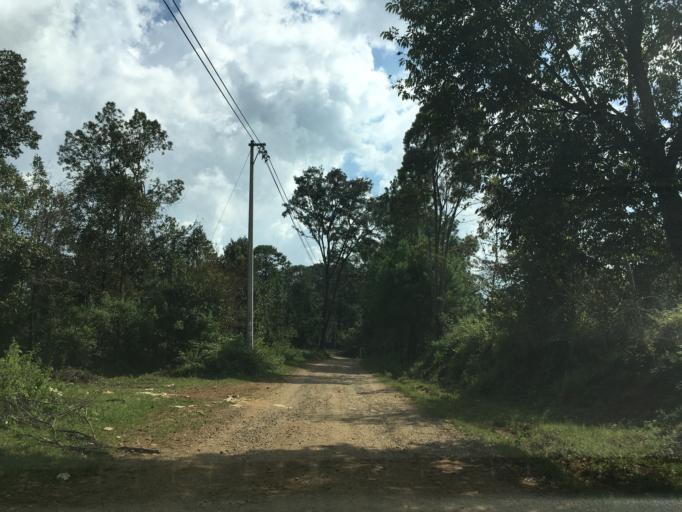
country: MX
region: Michoacan
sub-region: Morelia
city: Morelos
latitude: 19.5308
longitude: -101.2044
